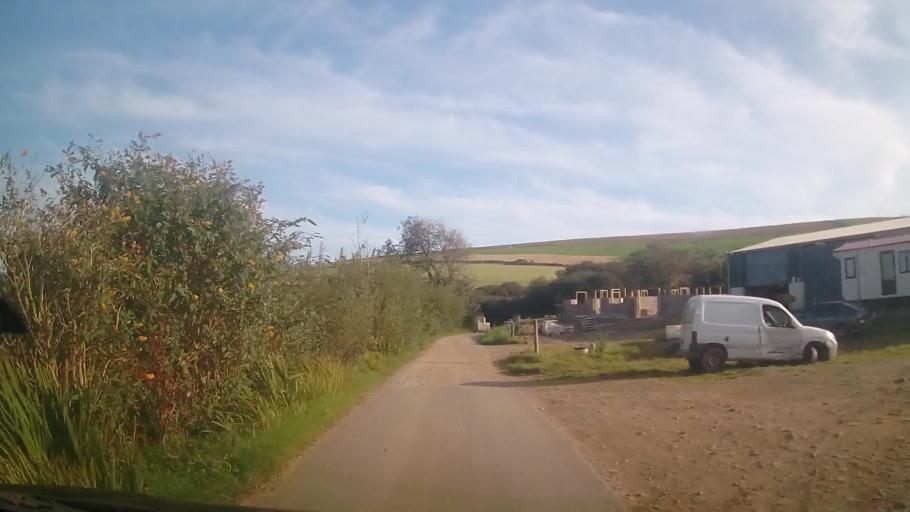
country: GB
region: Wales
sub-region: Pembrokeshire
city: Ambleston
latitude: 51.9649
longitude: -4.8937
